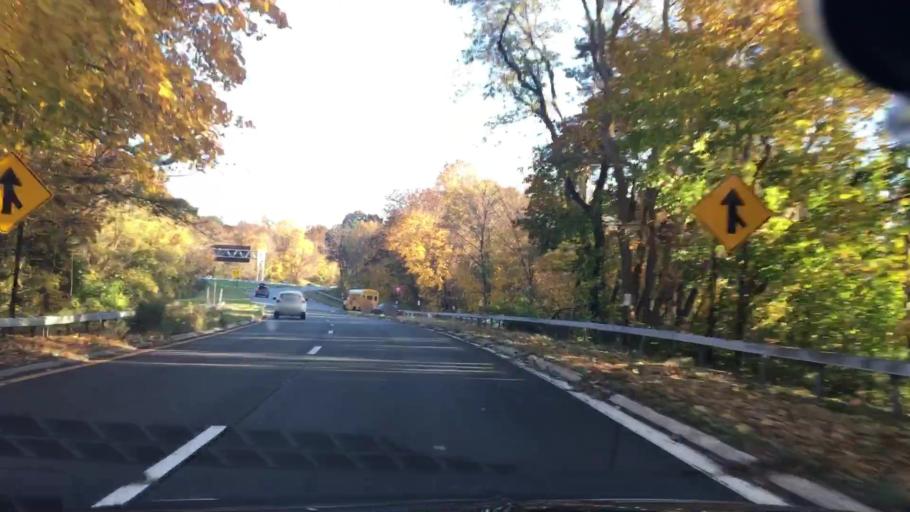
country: US
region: New York
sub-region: Westchester County
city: Hawthorne
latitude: 41.1071
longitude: -73.8004
